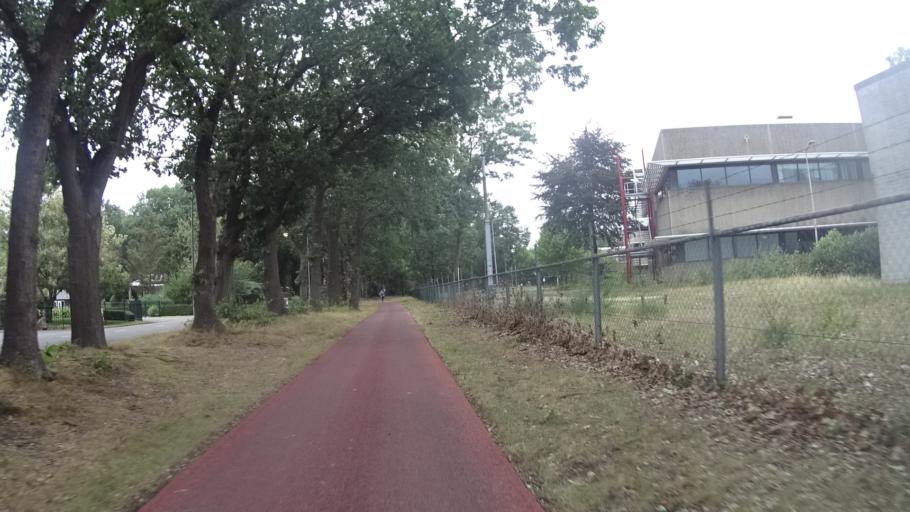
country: NL
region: Limburg
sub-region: Gemeente Venlo
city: Venlo
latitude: 51.3918
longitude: 6.1667
